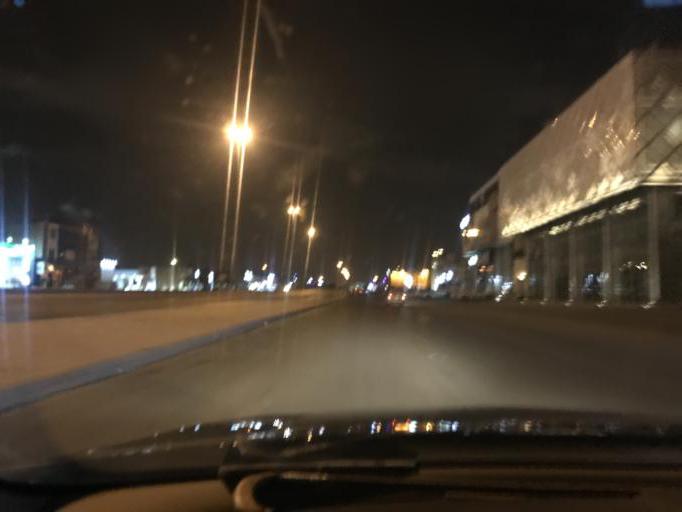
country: SA
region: Ar Riyad
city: Riyadh
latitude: 24.7958
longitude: 46.6986
